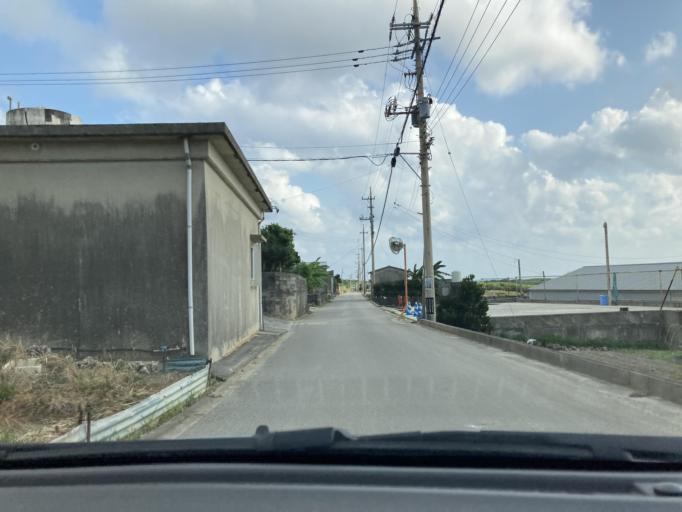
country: JP
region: Okinawa
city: Itoman
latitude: 26.0892
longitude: 127.6613
